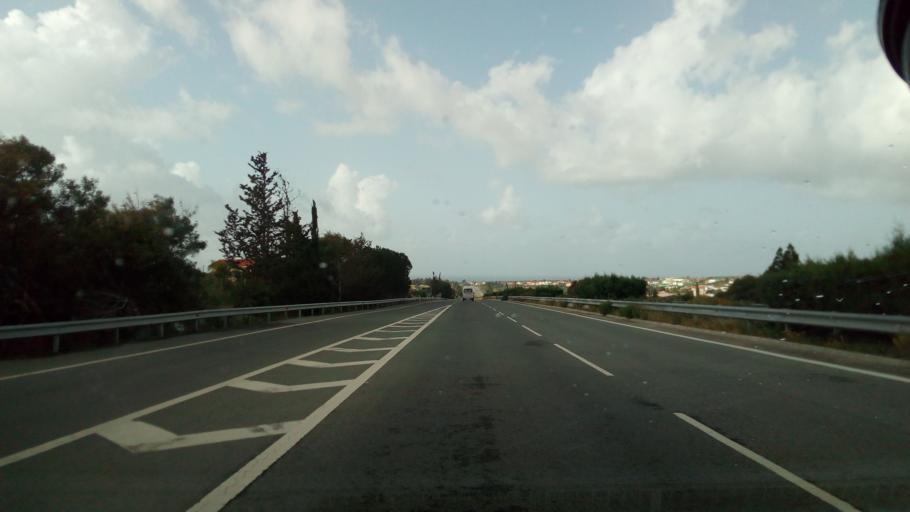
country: CY
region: Larnaka
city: Kolossi
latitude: 34.6833
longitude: 32.9353
